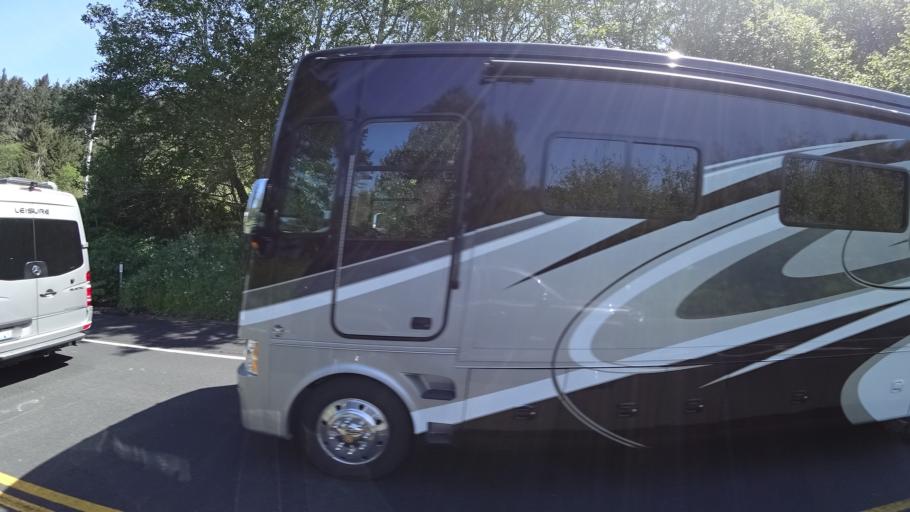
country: US
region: California
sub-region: Humboldt County
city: Westhaven-Moonstone
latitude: 41.2390
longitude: -124.0838
